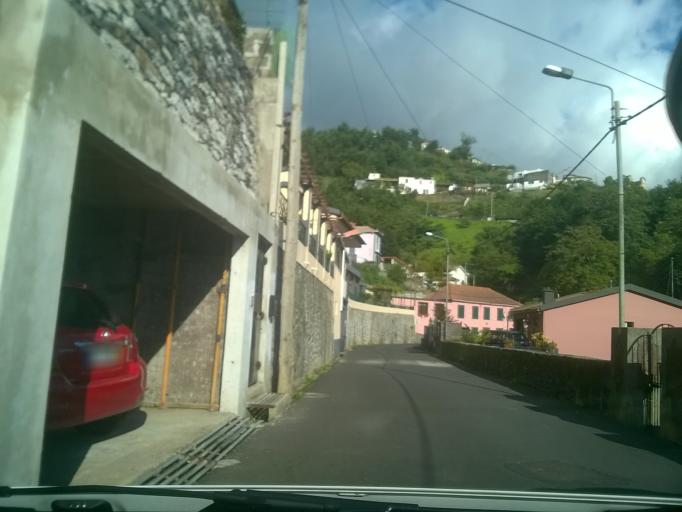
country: PT
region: Madeira
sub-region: Funchal
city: Nossa Senhora do Monte
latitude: 32.6783
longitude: -16.9035
